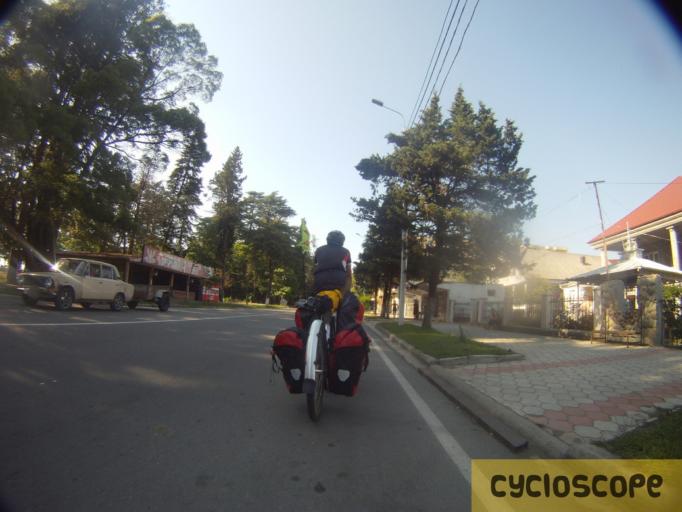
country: GE
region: Ajaria
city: Kobuleti
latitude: 41.8489
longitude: 41.7793
